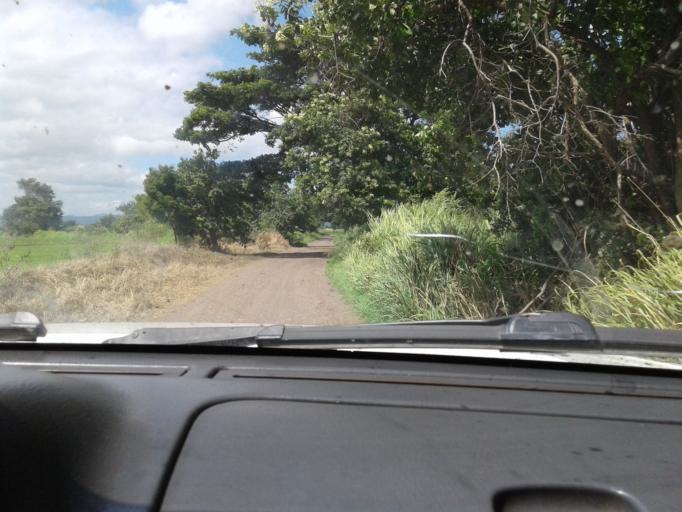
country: NI
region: Matagalpa
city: Ciudad Dario
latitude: 12.8447
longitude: -86.1426
